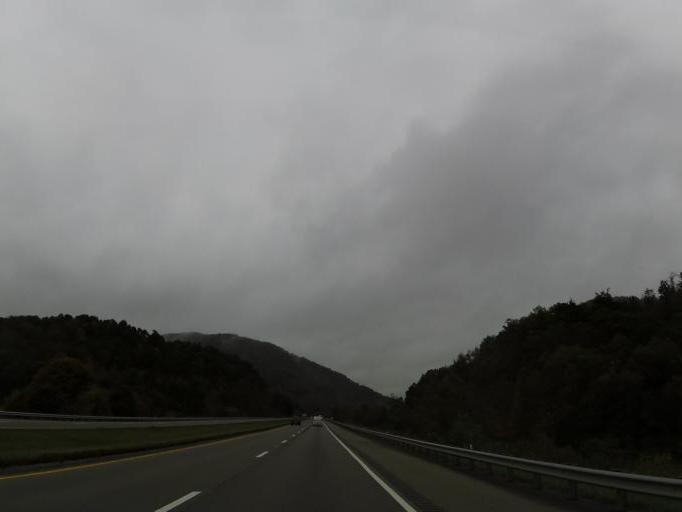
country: US
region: Virginia
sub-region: Wythe County
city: Wytheville
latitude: 37.0009
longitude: -81.0903
